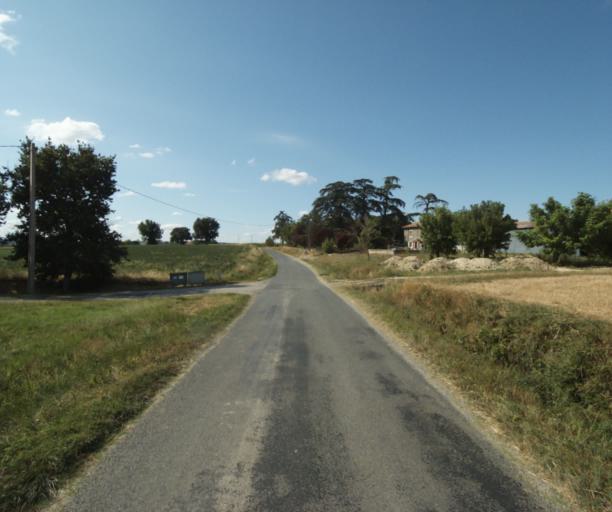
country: FR
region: Midi-Pyrenees
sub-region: Departement du Tarn
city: Puylaurens
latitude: 43.5312
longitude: 1.9735
